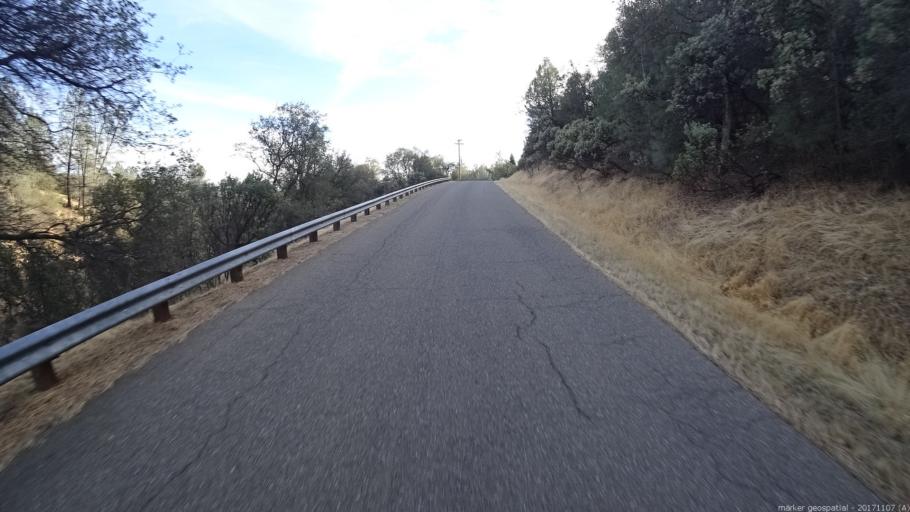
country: US
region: California
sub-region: Shasta County
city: Shasta
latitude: 40.5321
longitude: -122.4869
